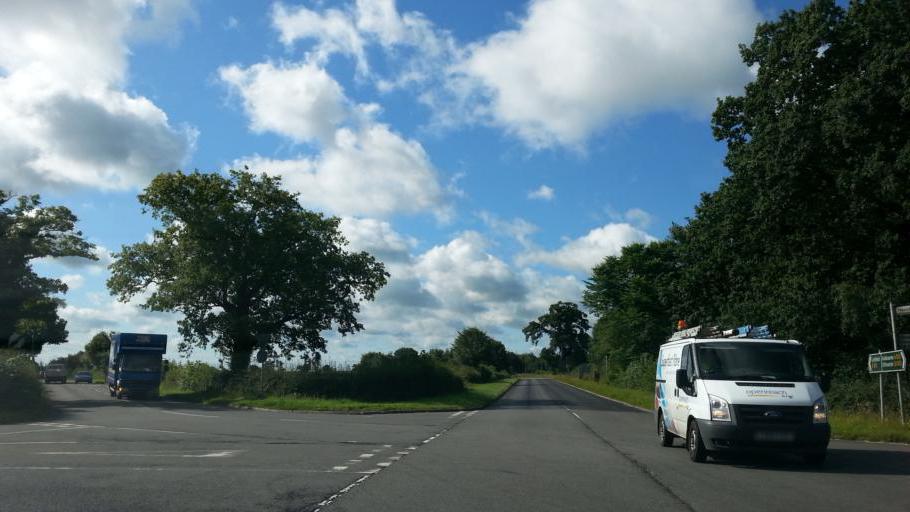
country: GB
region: England
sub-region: Staffordshire
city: Barton under Needwood
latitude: 52.8450
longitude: -1.7777
